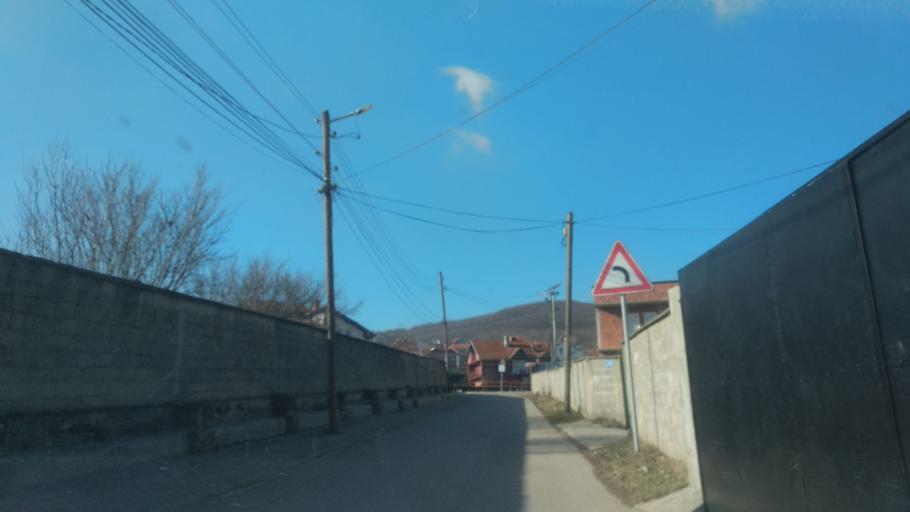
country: XK
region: Pristina
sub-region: Komuna e Gracanices
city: Glanica
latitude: 42.5842
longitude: 21.0037
